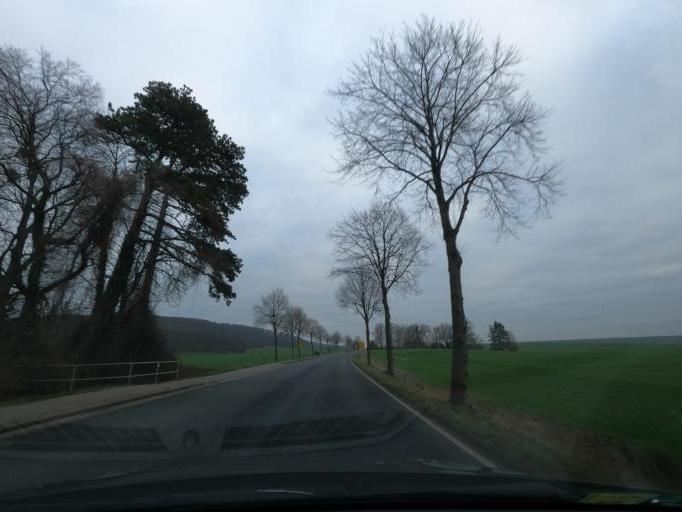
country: DE
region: Lower Saxony
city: Wittmar
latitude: 52.1419
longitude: 10.6162
